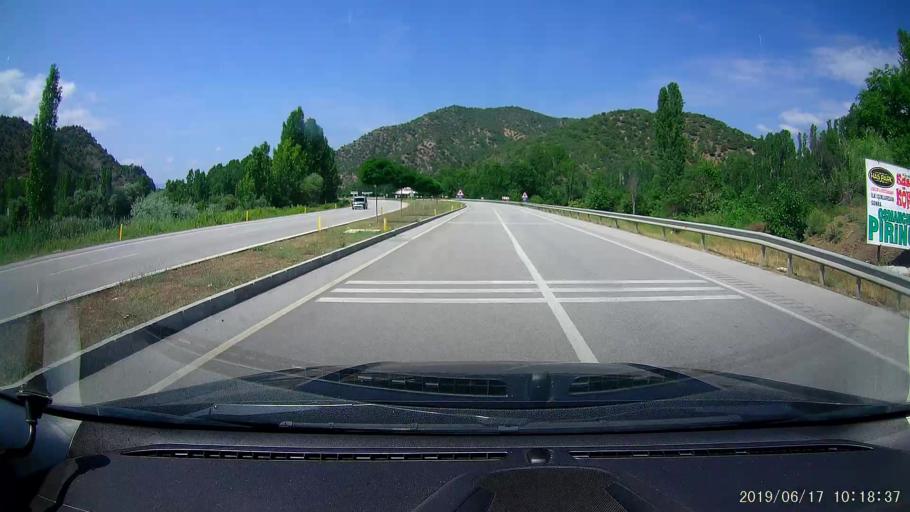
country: TR
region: Corum
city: Osmancik
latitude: 40.9775
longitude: 34.9171
